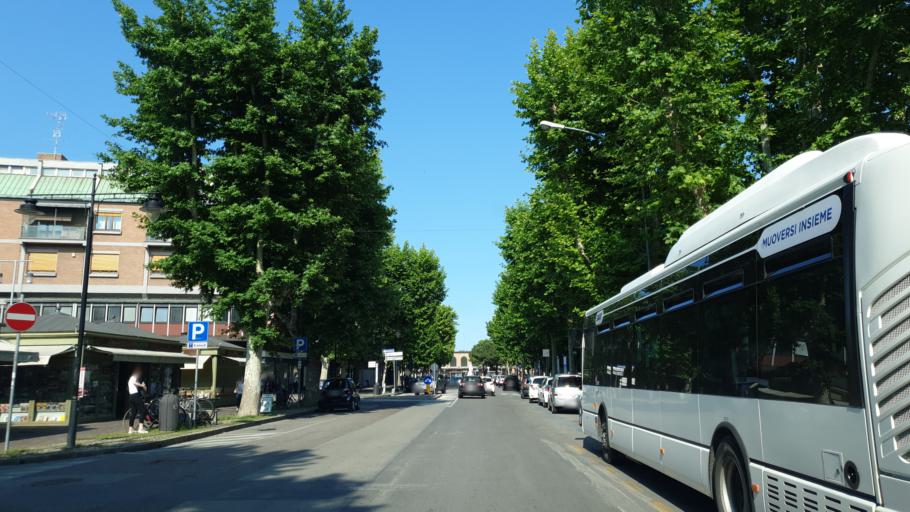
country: IT
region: Emilia-Romagna
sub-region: Provincia di Ravenna
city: Ravenna
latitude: 44.4186
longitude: 12.2049
